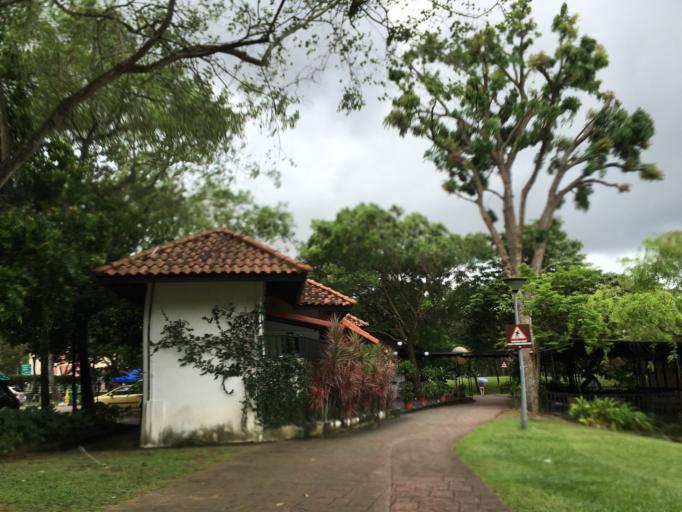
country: SG
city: Singapore
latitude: 1.3751
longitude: 103.8986
